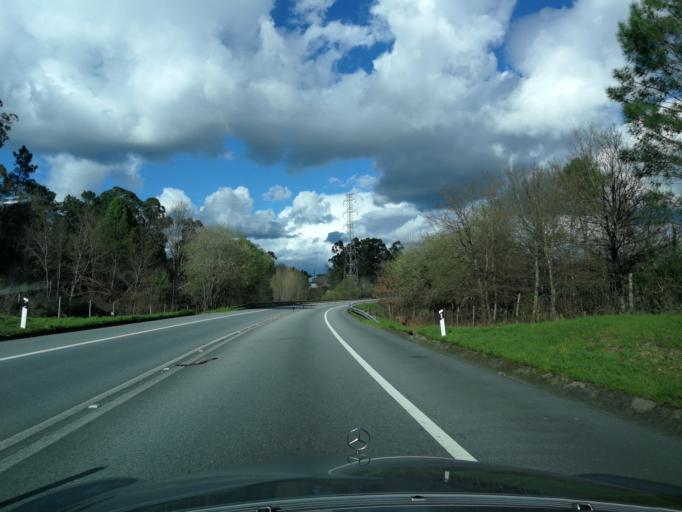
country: PT
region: Braga
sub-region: Vila Verde
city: Prado
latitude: 41.6151
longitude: -8.4517
